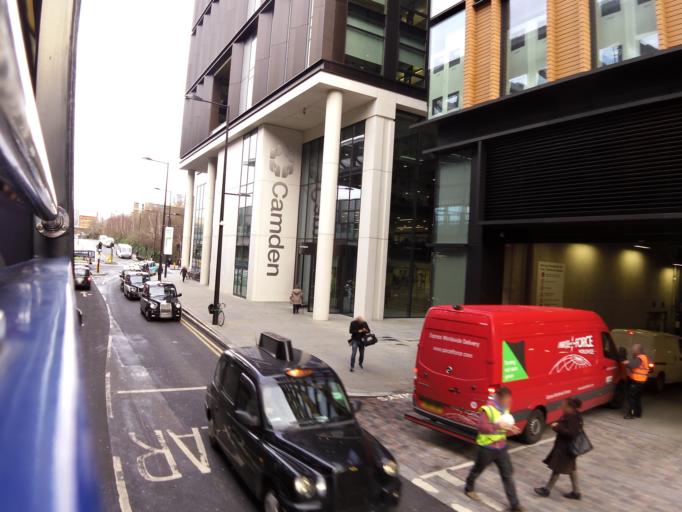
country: GB
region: England
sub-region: Greater London
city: Barnsbury
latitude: 51.5332
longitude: -0.1264
